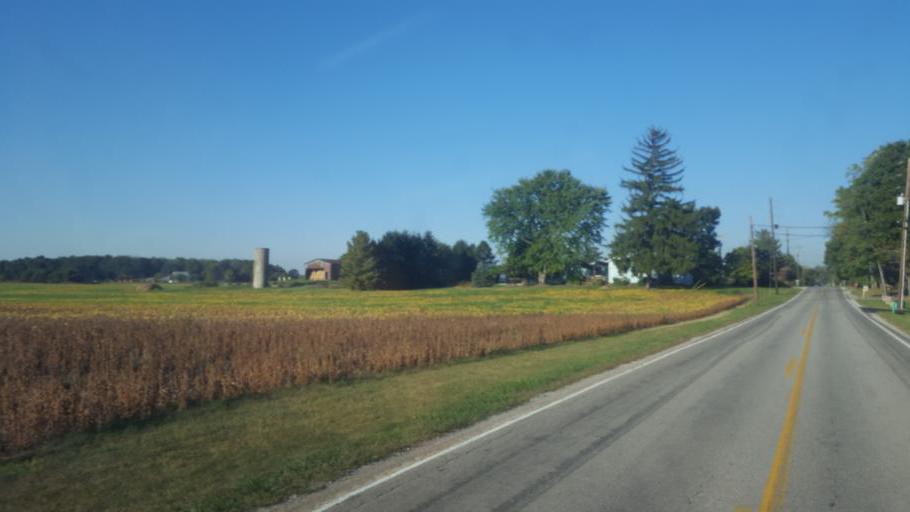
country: US
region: Ohio
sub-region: Marion County
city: Marion
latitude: 40.5494
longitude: -83.1234
